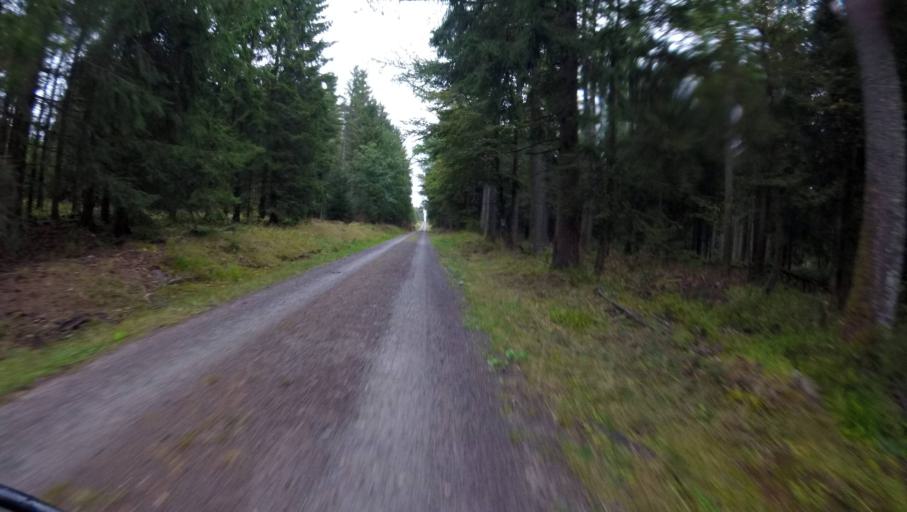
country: DE
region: Baden-Wuerttemberg
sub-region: Karlsruhe Region
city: Forbach
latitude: 48.6841
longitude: 8.4178
